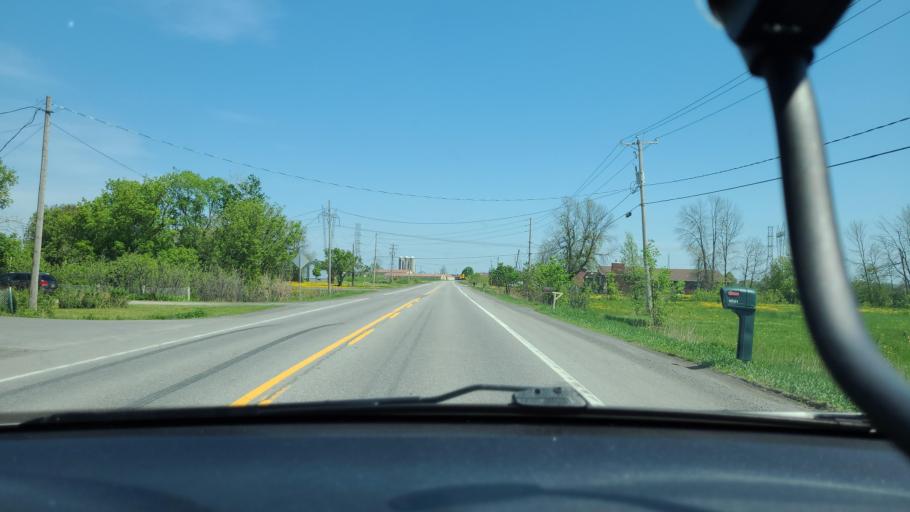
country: CA
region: Quebec
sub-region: Laurentides
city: Mirabel
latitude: 45.6016
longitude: -74.0521
